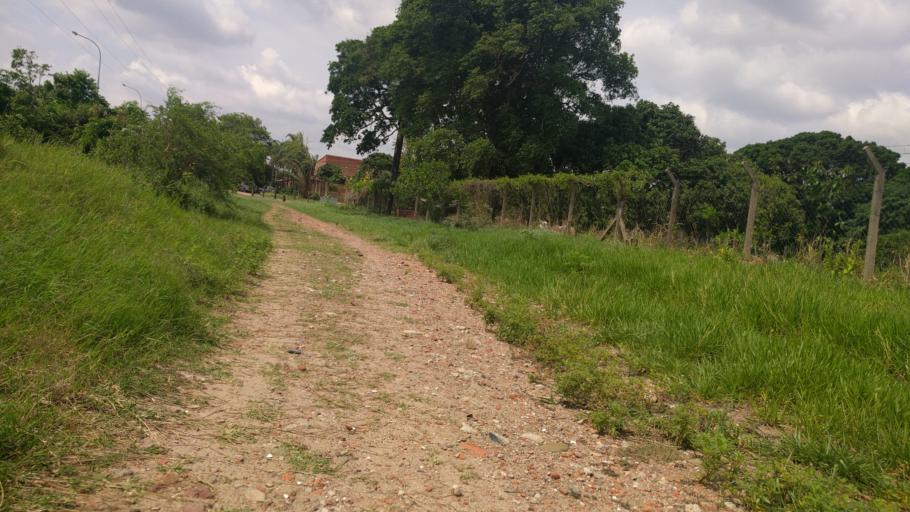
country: BO
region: Santa Cruz
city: Santa Cruz de la Sierra
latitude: -17.7948
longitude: -63.2227
